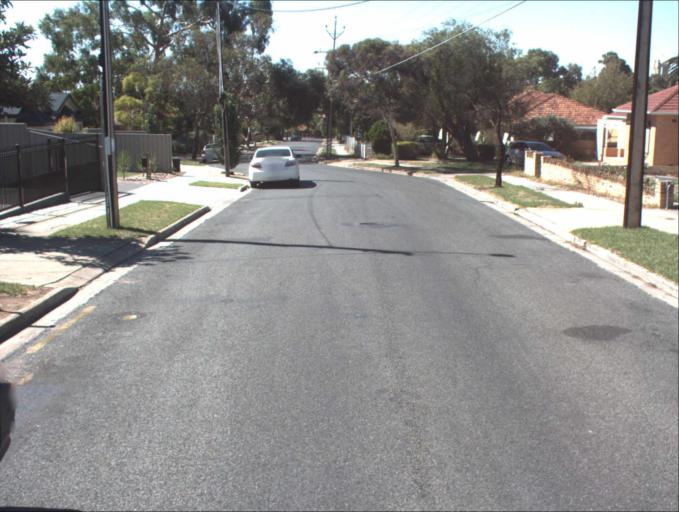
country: AU
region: South Australia
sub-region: Port Adelaide Enfield
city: Blair Athol
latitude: -34.8663
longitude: 138.6057
